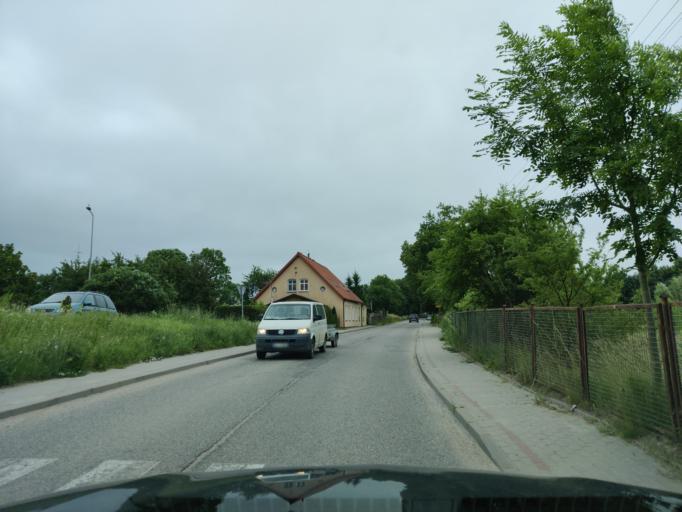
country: PL
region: Warmian-Masurian Voivodeship
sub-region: Powiat gizycki
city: Ryn
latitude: 53.9339
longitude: 21.5495
